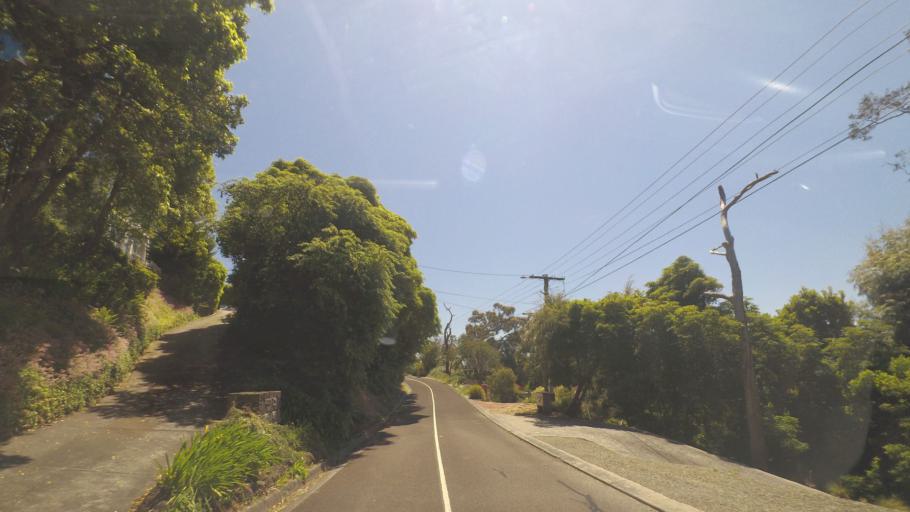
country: AU
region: Victoria
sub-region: Maroondah
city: Croydon Hills
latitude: -37.7816
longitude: 145.2791
